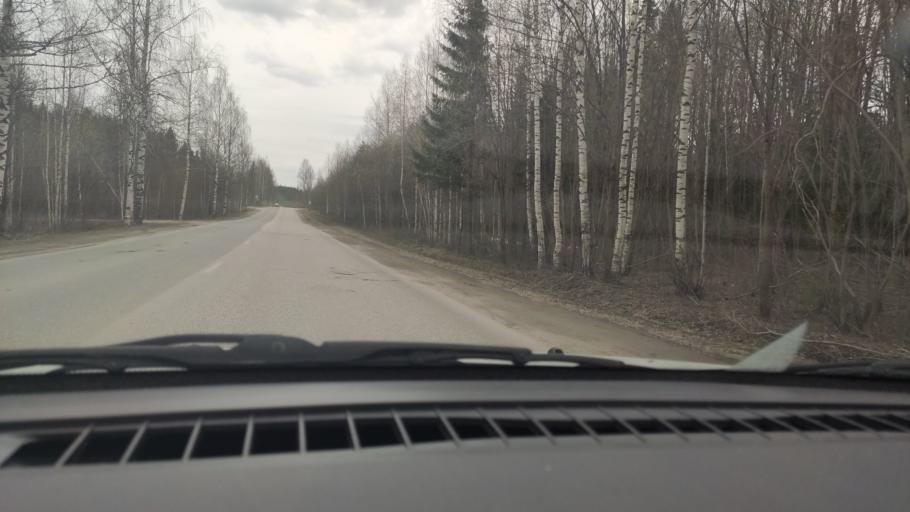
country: RU
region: Perm
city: Polazna
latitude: 58.1050
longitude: 56.4166
